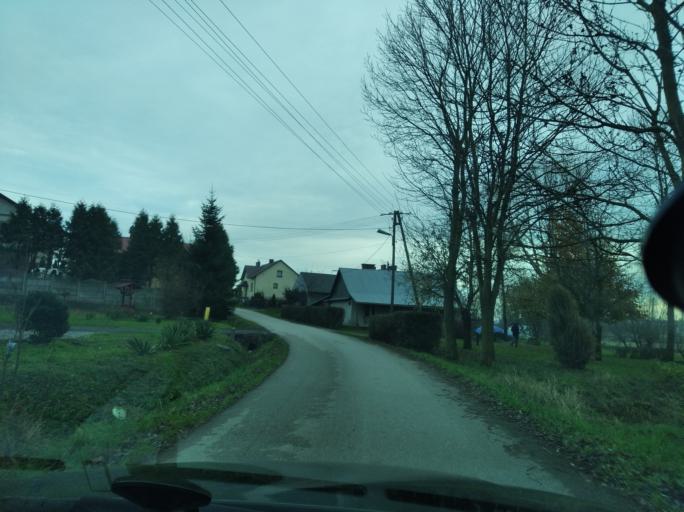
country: PL
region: Subcarpathian Voivodeship
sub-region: Powiat przeworski
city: Debow
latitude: 50.0494
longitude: 22.4311
